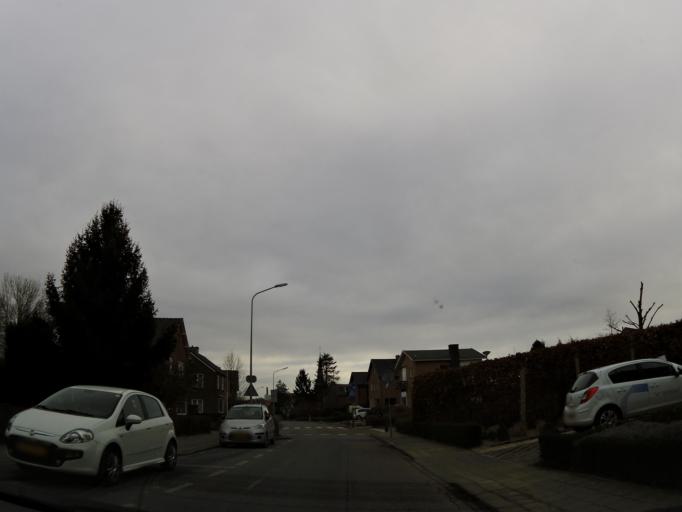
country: NL
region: Limburg
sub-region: Gemeente Onderbanken
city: Schinveld
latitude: 50.9721
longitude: 5.9746
